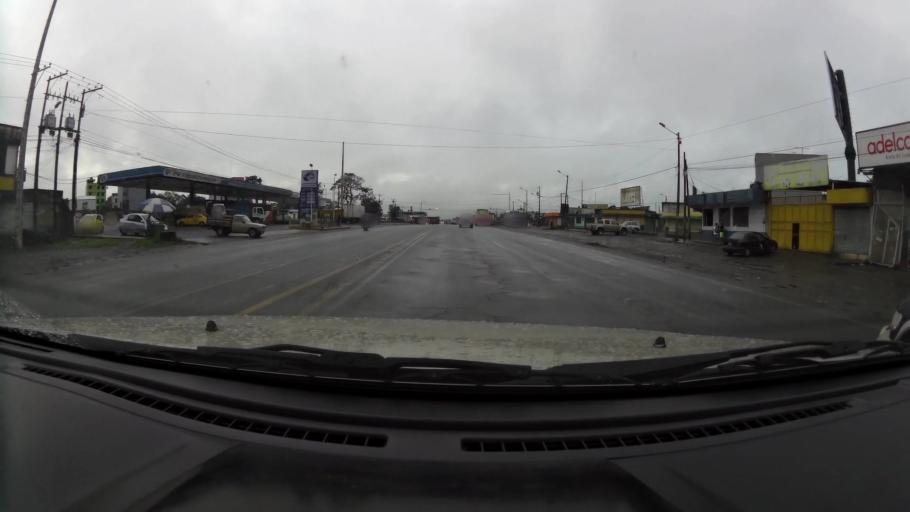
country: EC
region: Santo Domingo de los Tsachilas
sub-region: Canton Santo Domingo de los Colorados
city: Santo Domingo de los Colorados
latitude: -0.2347
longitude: -79.1690
